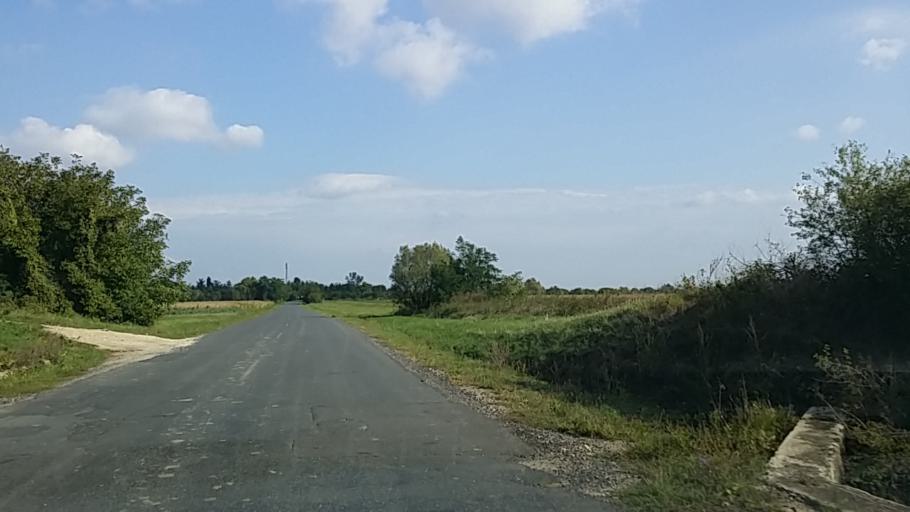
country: HU
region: Vas
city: Csepreg
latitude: 47.3854
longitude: 16.7151
